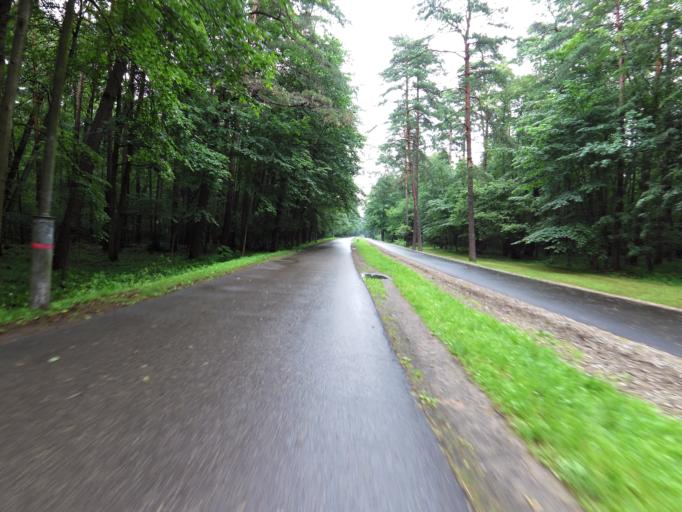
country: LT
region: Vilnius County
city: Vilkpede
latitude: 54.6866
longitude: 25.2354
